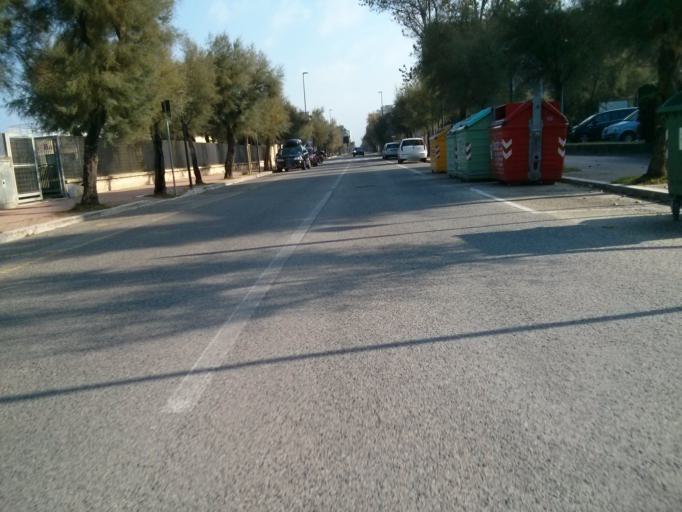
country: IT
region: The Marches
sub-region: Provincia di Pesaro e Urbino
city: Pesaro
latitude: 43.9216
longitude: 12.9070
